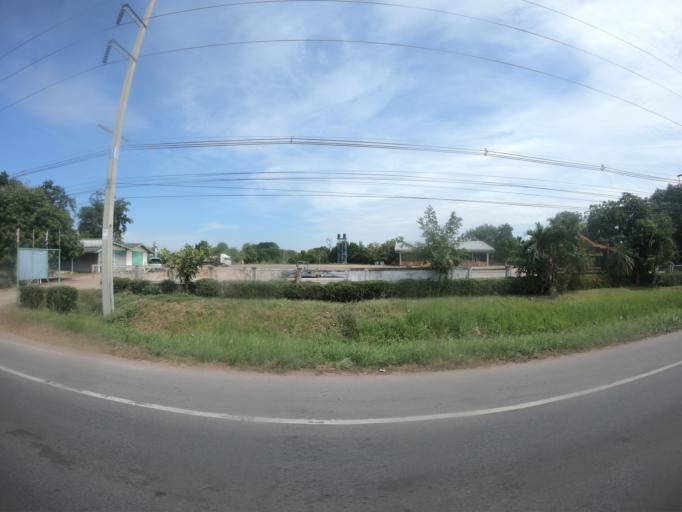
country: TH
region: Maha Sarakham
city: Chiang Yuen
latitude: 16.4448
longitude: 103.0389
